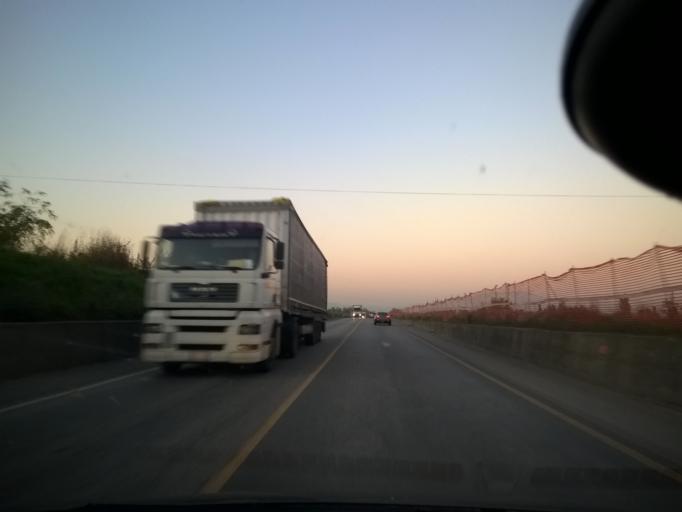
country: IT
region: Lombardy
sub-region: Provincia di Brescia
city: Ospitaletto
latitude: 45.5480
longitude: 10.0546
